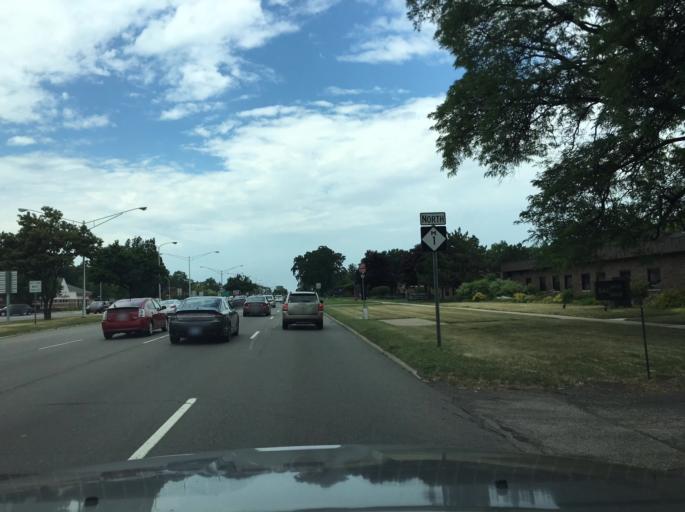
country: US
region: Michigan
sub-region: Oakland County
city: Royal Oak
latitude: 42.4830
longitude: -83.1525
